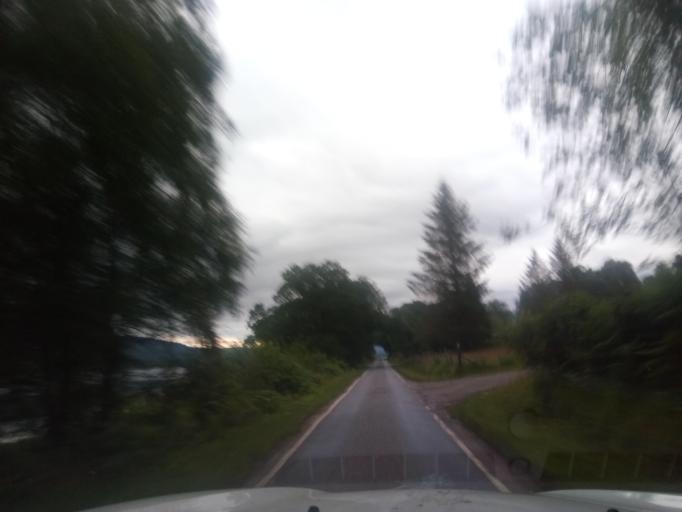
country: GB
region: Scotland
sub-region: Highland
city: Fort William
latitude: 56.8468
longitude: -5.2908
